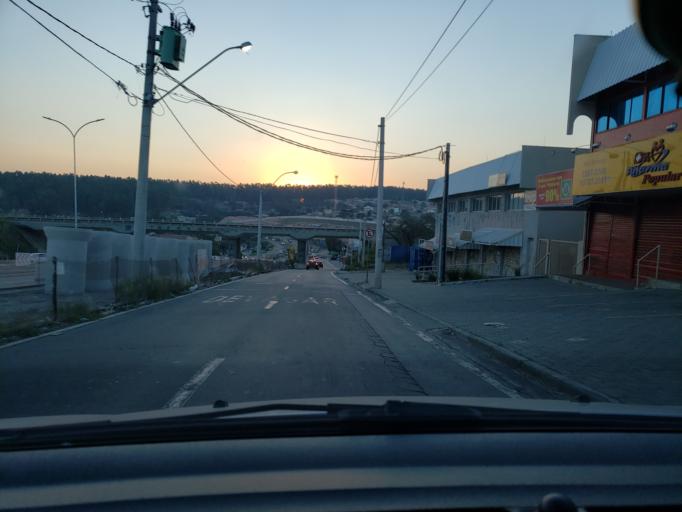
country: BR
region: Sao Paulo
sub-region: Hortolandia
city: Hortolandia
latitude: -22.9372
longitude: -47.1589
